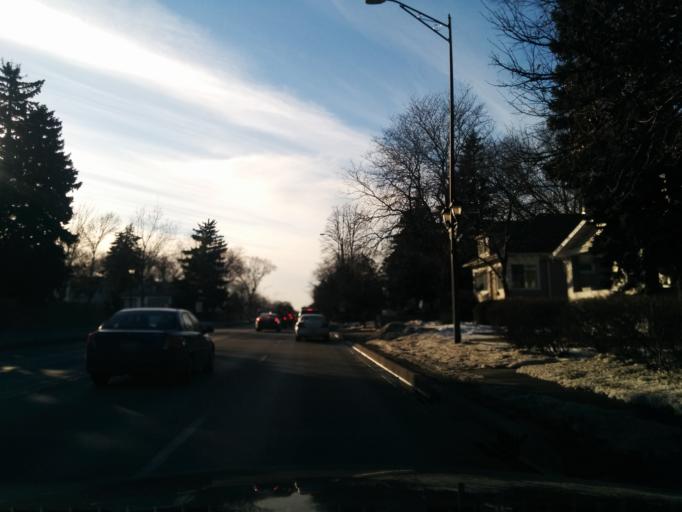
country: US
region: Illinois
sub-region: DuPage County
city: Elmhurst
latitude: 41.9064
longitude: -87.9360
